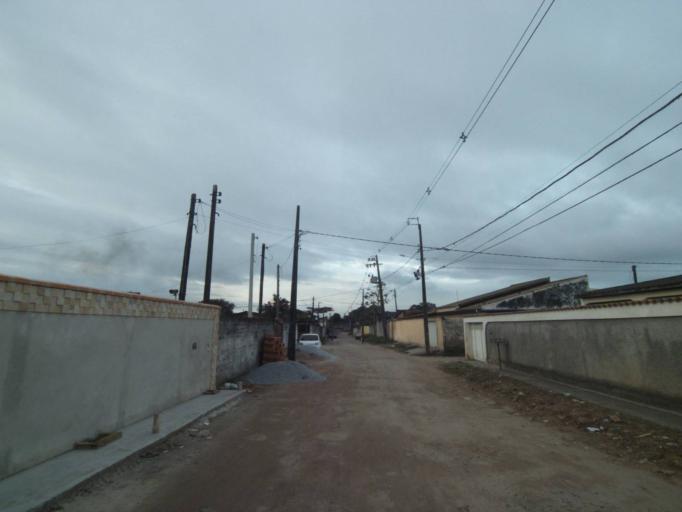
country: BR
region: Parana
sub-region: Paranagua
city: Paranagua
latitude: -25.5354
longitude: -48.5477
